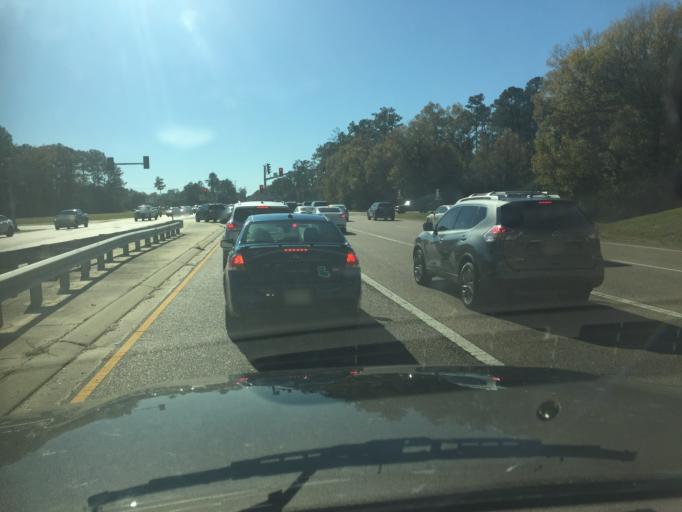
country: US
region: Louisiana
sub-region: Saint Tammany Parish
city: Covington
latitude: 30.4471
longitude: -90.1407
